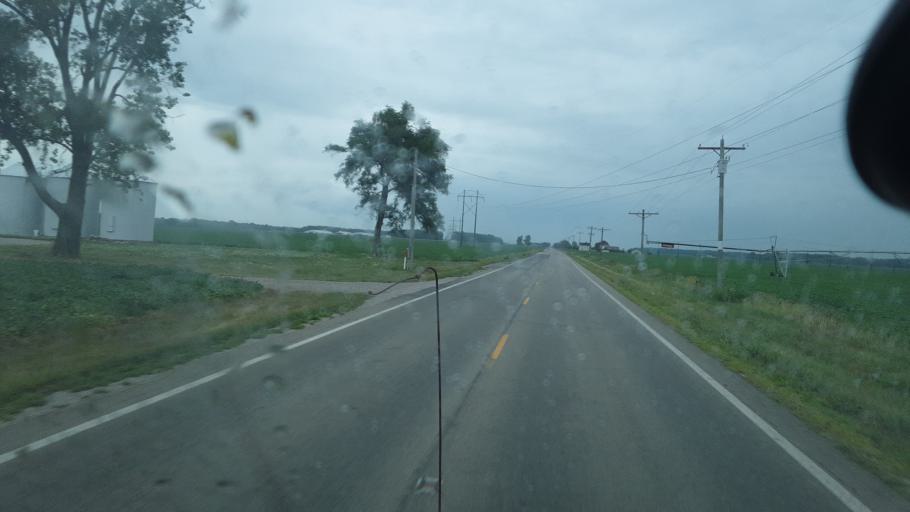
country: US
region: Ohio
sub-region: Defiance County
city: Hicksville
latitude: 41.2961
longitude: -84.6871
